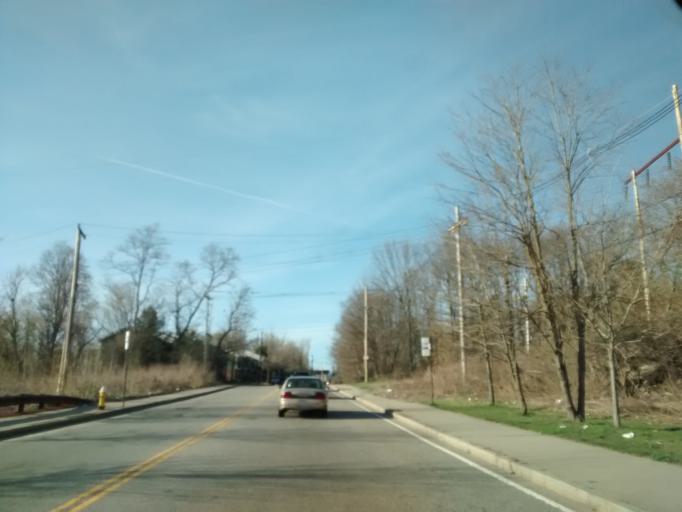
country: US
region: Massachusetts
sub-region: Worcester County
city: Sunderland
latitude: 42.2377
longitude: -71.7922
